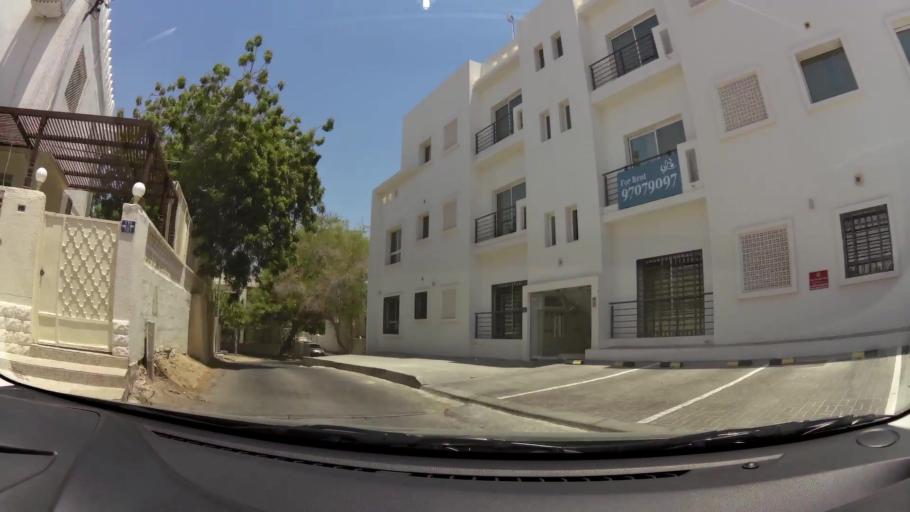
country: OM
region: Muhafazat Masqat
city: Muscat
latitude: 23.6053
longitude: 58.5438
